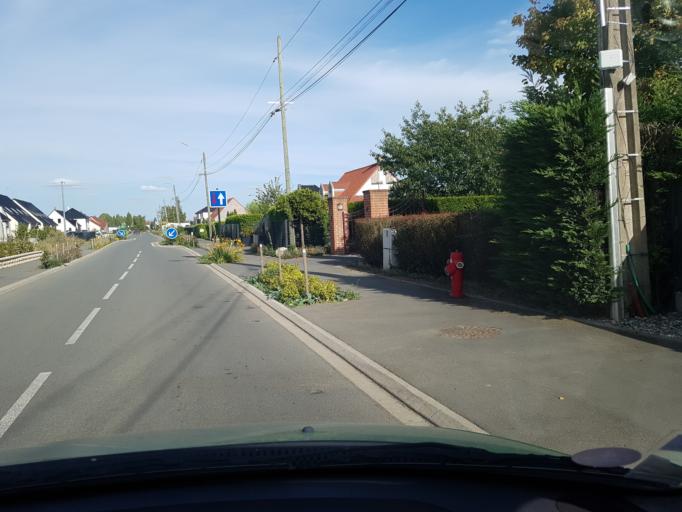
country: FR
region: Nord-Pas-de-Calais
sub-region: Departement du Pas-de-Calais
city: Hinges
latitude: 50.5912
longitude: 2.6343
